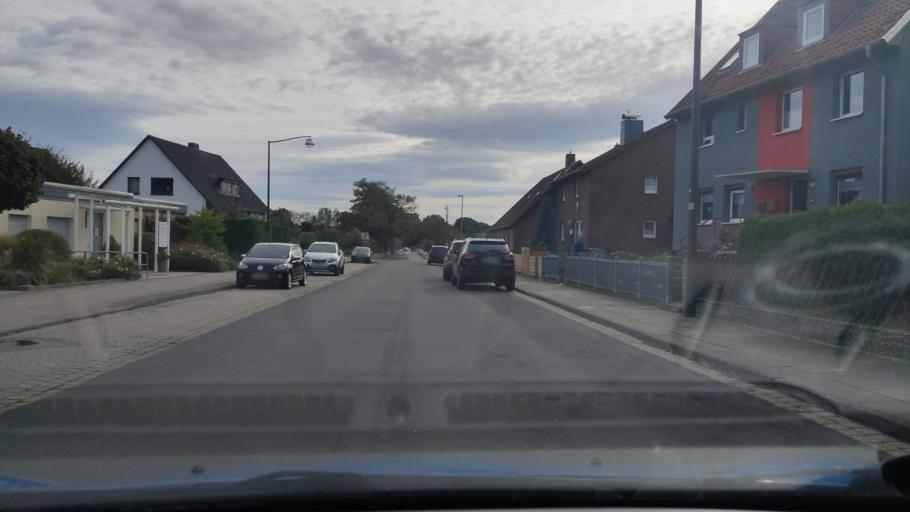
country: DE
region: Lower Saxony
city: Langenhagen
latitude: 52.4369
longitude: 9.6991
